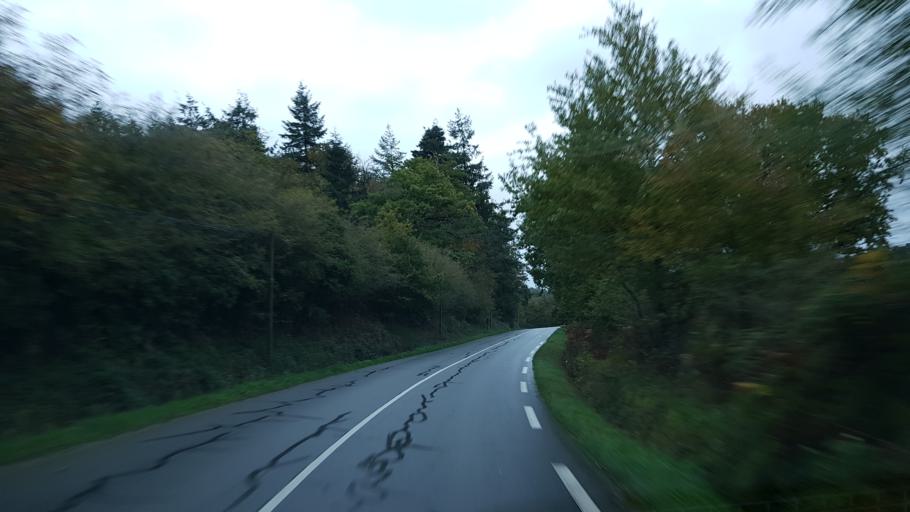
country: FR
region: Brittany
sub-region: Departement d'Ille-et-Vilaine
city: Vitre
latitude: 48.1358
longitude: -1.1807
